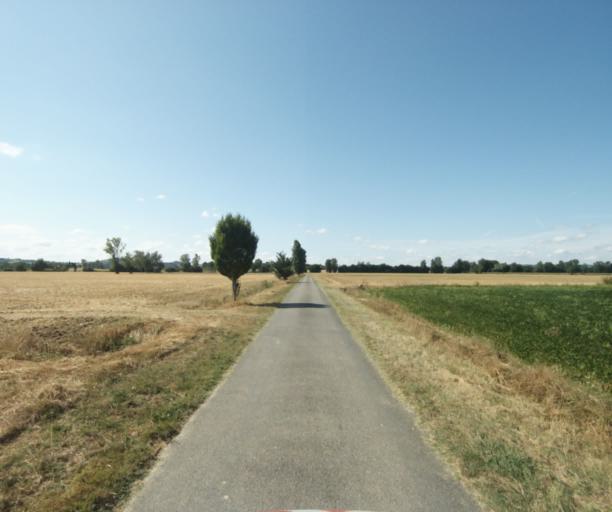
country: FR
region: Midi-Pyrenees
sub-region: Departement de la Haute-Garonne
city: Revel
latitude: 43.4943
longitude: 1.9871
